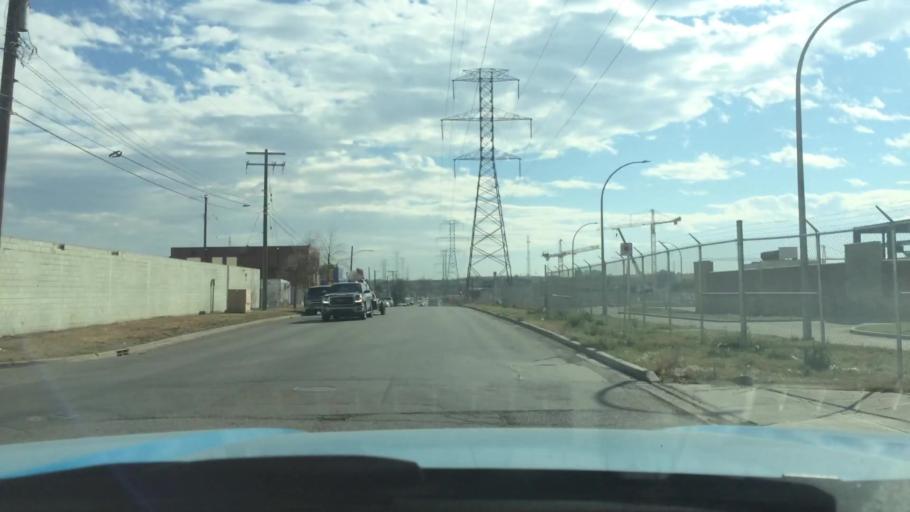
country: CA
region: Alberta
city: Calgary
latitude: 51.0155
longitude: -114.0238
